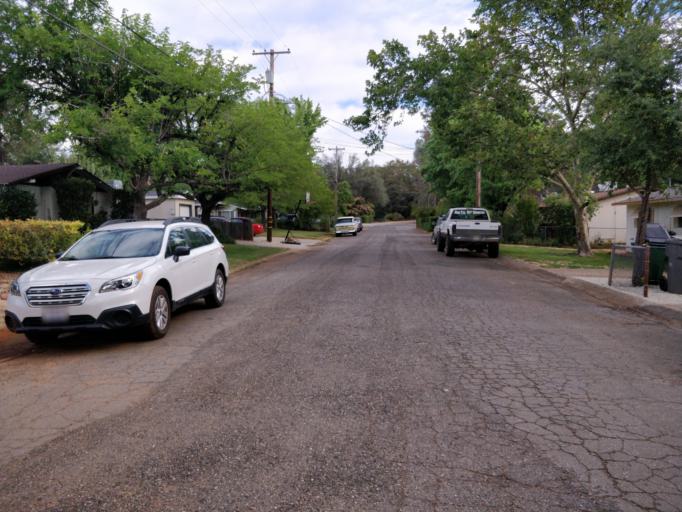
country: US
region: California
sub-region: Shasta County
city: Shasta Lake
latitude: 40.6866
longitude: -122.3572
